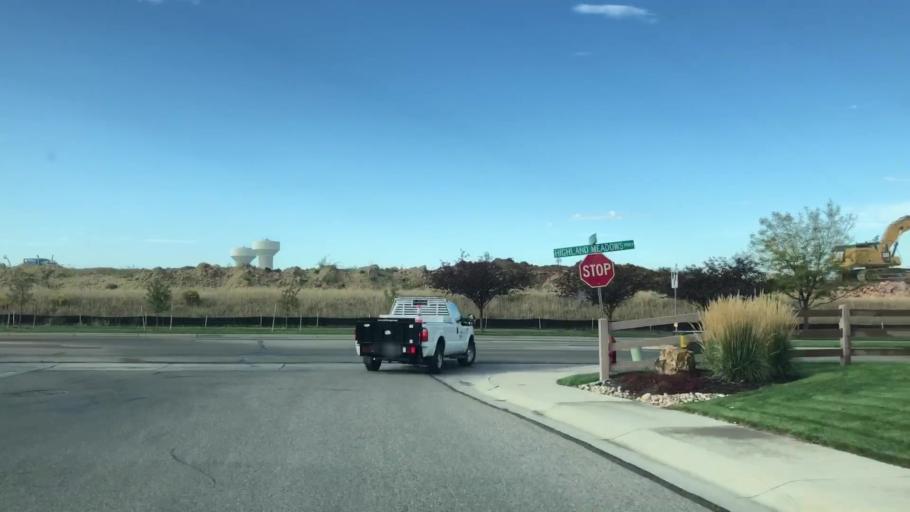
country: US
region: Colorado
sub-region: Weld County
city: Windsor
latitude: 40.4432
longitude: -104.9698
